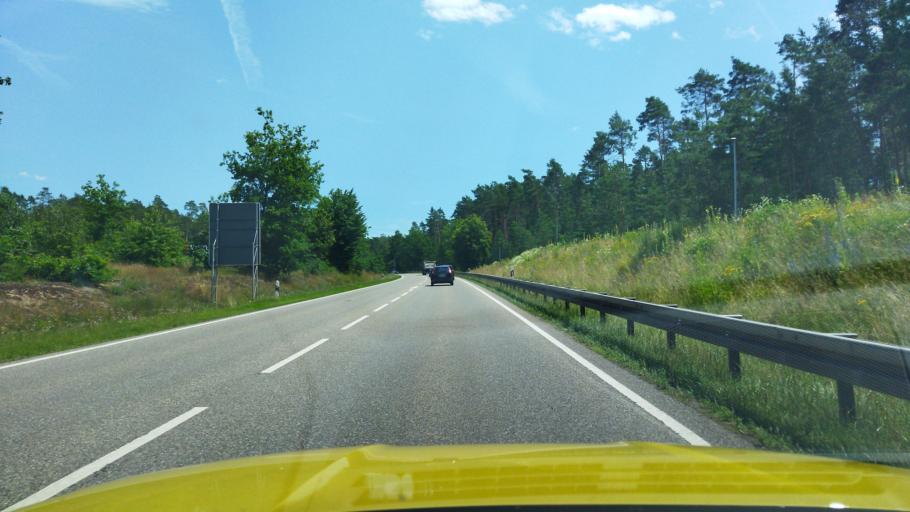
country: DE
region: Bavaria
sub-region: Regierungsbezirk Mittelfranken
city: Roth
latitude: 49.2442
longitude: 11.1207
